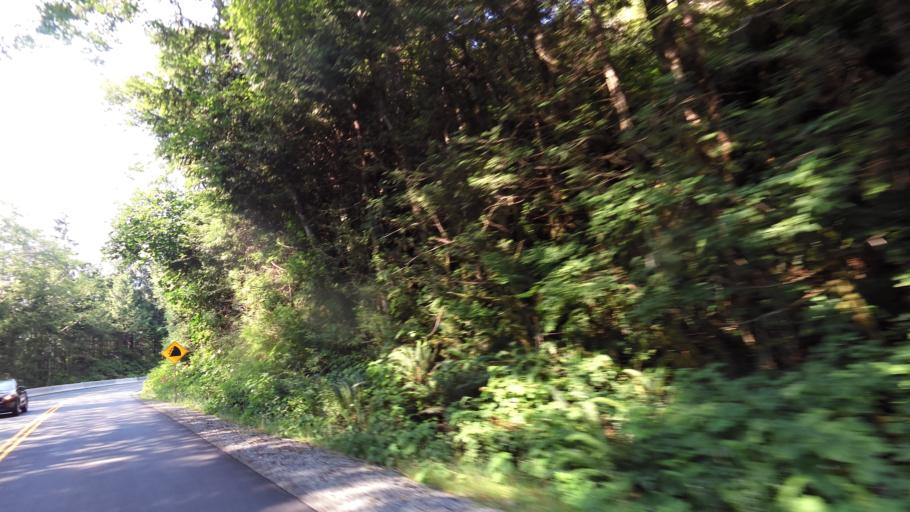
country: CA
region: British Columbia
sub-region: Regional District of Alberni-Clayoquot
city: Ucluelet
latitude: 49.0941
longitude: -125.4521
